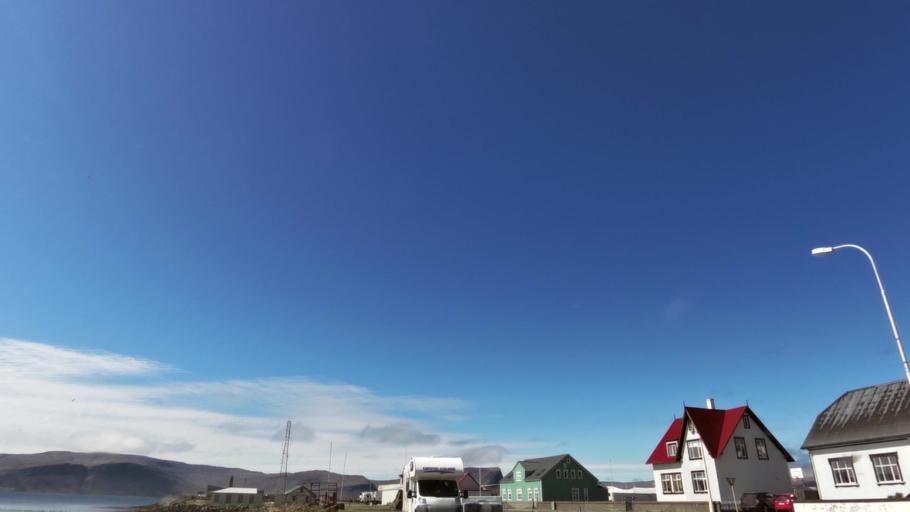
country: IS
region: West
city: Olafsvik
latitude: 65.5968
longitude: -23.9978
